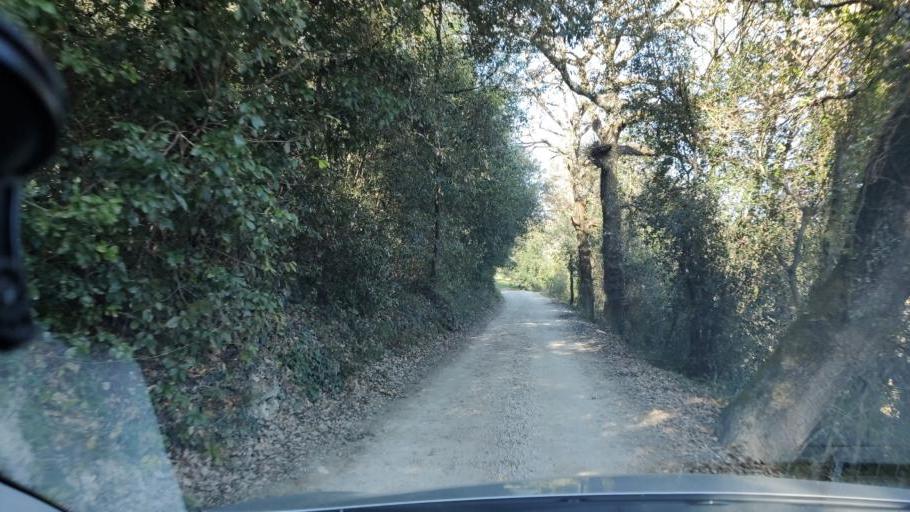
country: IT
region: Umbria
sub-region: Provincia di Terni
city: Fornole
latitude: 42.5539
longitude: 12.4446
